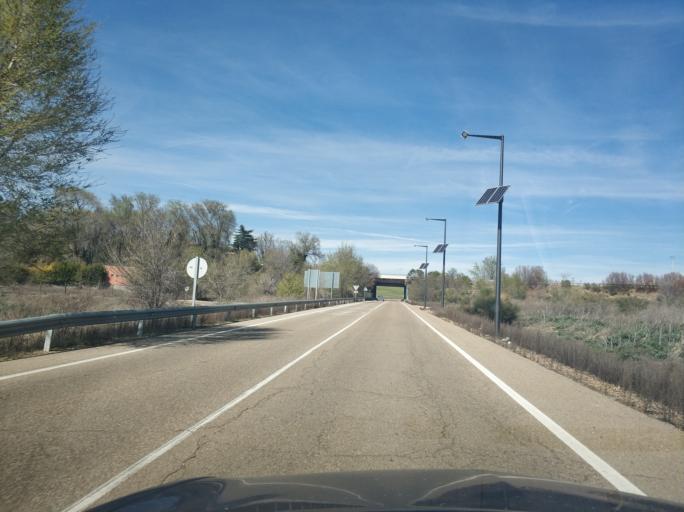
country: ES
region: Castille and Leon
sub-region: Provincia de Valladolid
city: Simancas
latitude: 41.5961
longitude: -4.8200
